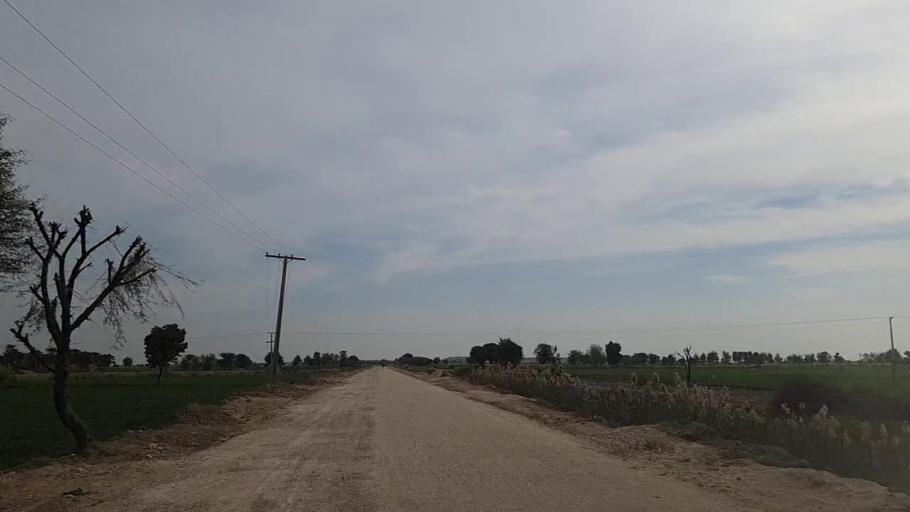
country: PK
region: Sindh
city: Jam Sahib
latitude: 26.4098
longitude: 68.4924
